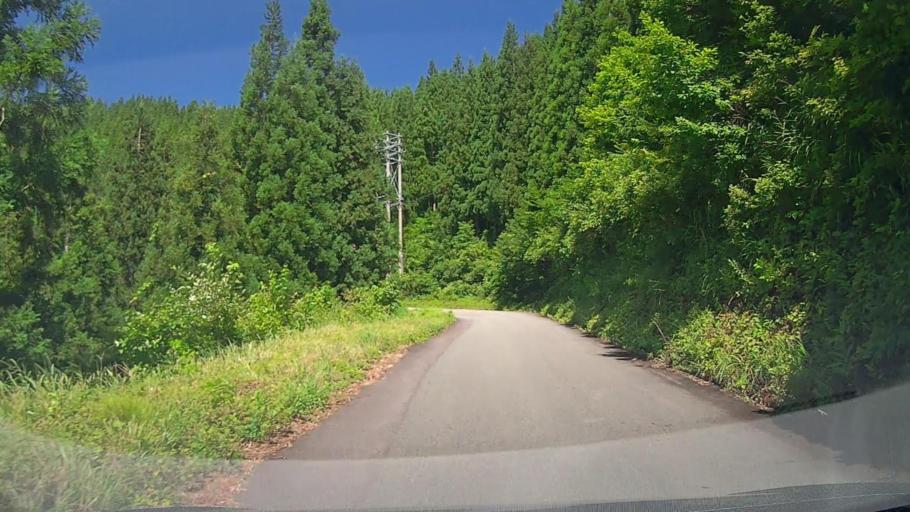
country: JP
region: Nagano
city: Iiyama
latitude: 36.9338
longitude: 138.4625
